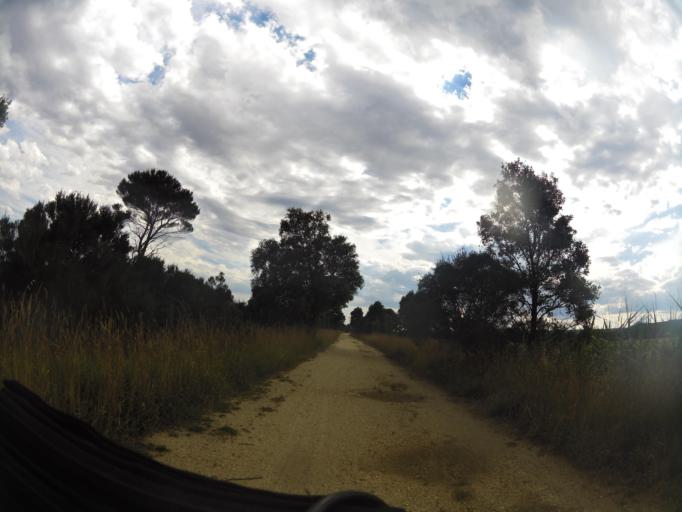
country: AU
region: Victoria
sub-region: Wellington
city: Heyfield
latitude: -38.0466
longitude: 146.6369
